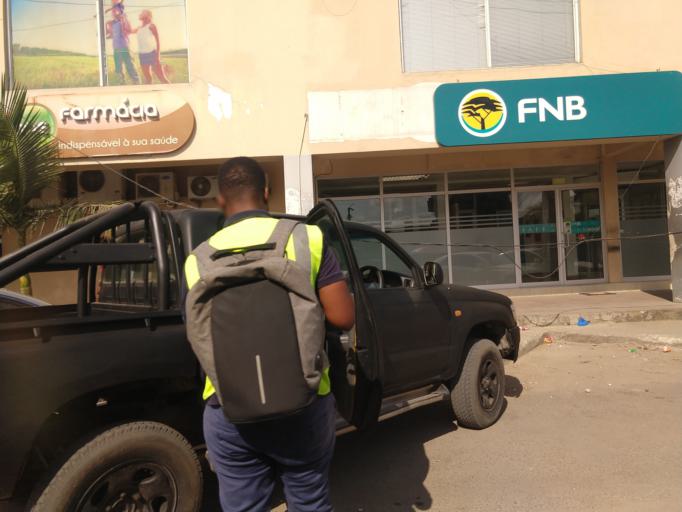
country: MZ
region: Sofala
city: Beira
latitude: -19.8300
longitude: 34.8415
